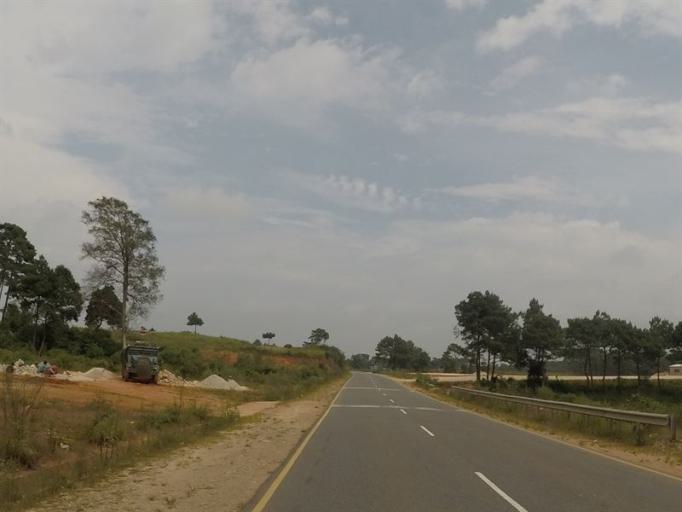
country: IN
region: Meghalaya
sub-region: East Khasi Hills
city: Shillong
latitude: 25.4908
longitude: 92.1849
